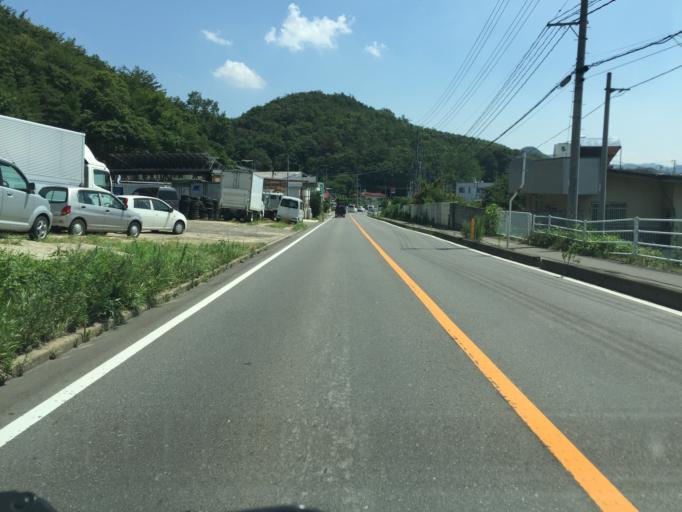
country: JP
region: Fukushima
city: Hobaramachi
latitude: 37.7988
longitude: 140.5172
